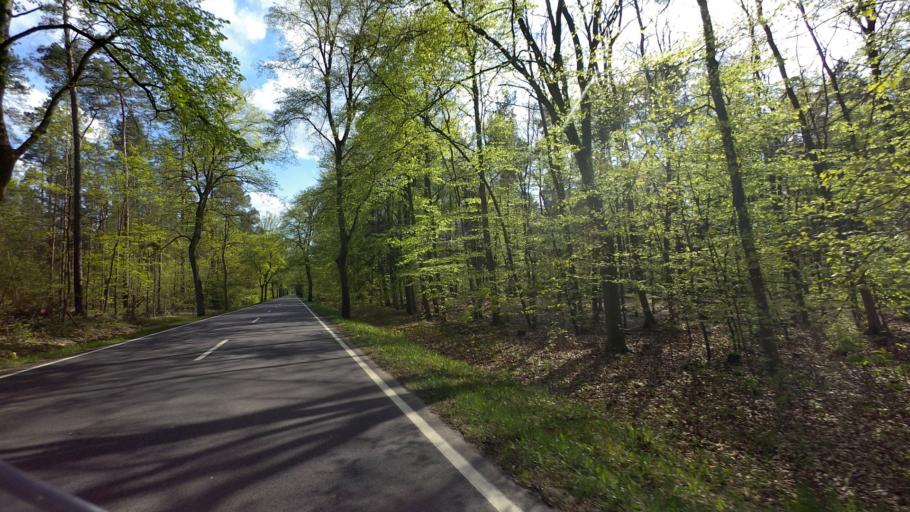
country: DE
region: Brandenburg
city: Milmersdorf
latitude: 53.0137
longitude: 13.6014
